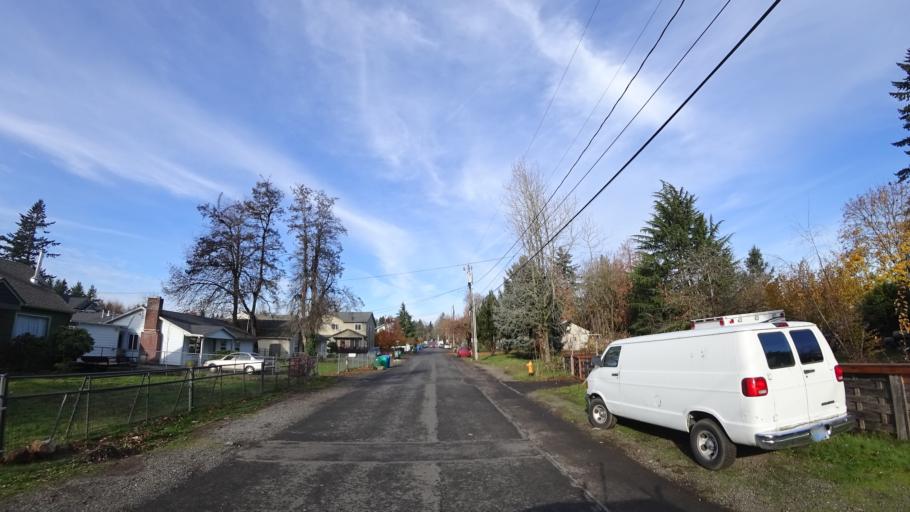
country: US
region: Oregon
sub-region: Multnomah County
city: Lents
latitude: 45.5204
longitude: -122.5159
